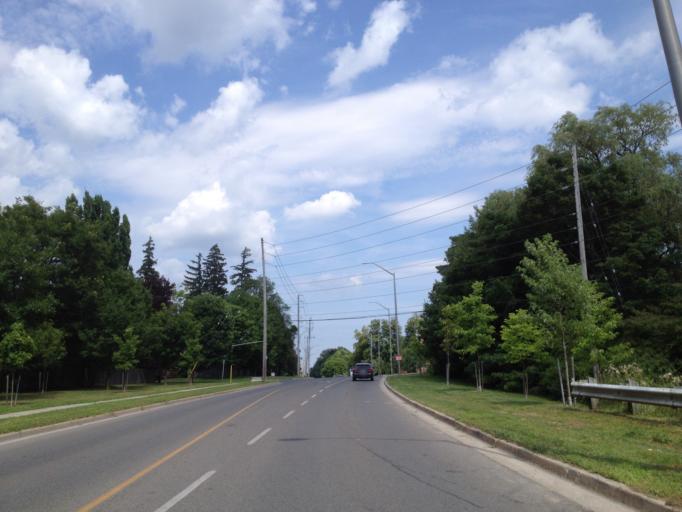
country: CA
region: Ontario
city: London
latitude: 43.0178
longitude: -81.2674
